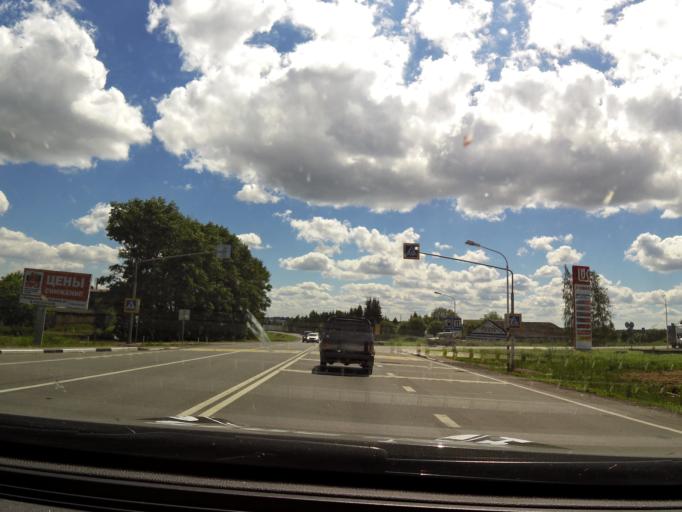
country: RU
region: Vologda
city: Molochnoye
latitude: 59.2900
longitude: 39.6902
